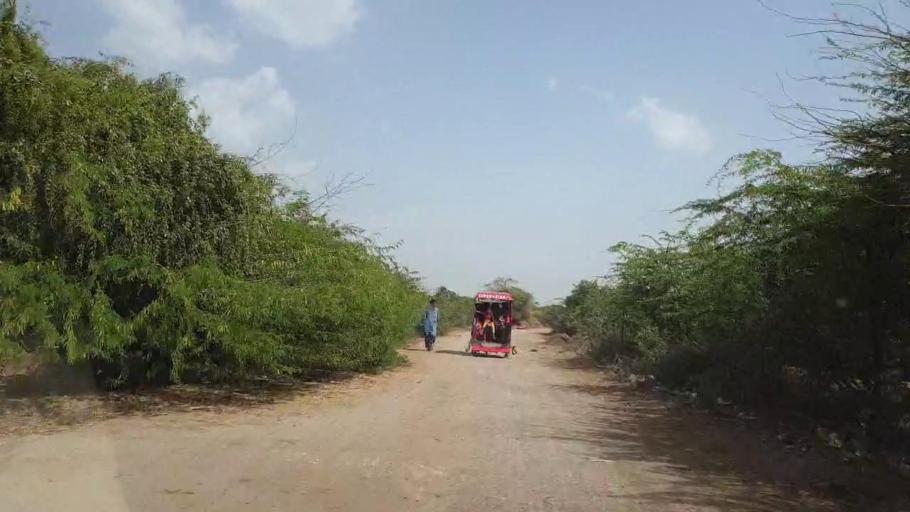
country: PK
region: Sindh
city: Rajo Khanani
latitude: 25.0505
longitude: 68.8651
